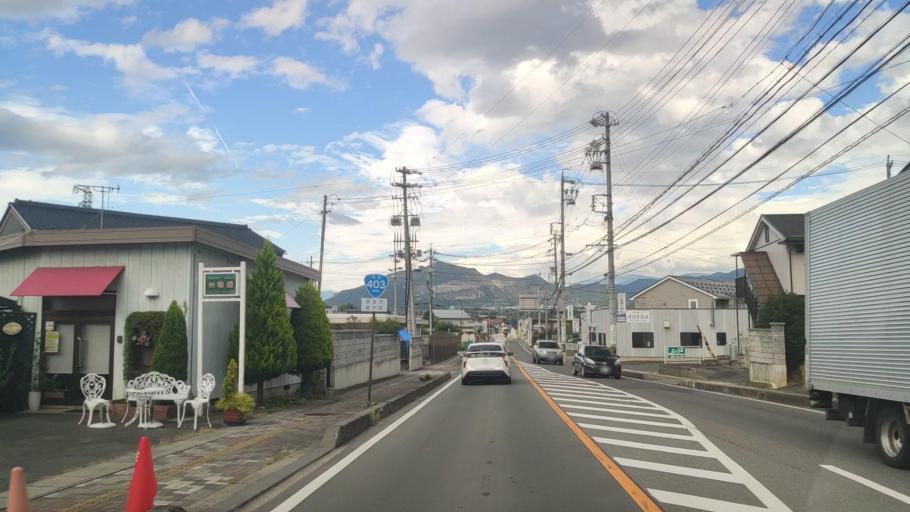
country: JP
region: Nagano
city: Suzaka
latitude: 36.6590
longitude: 138.3122
